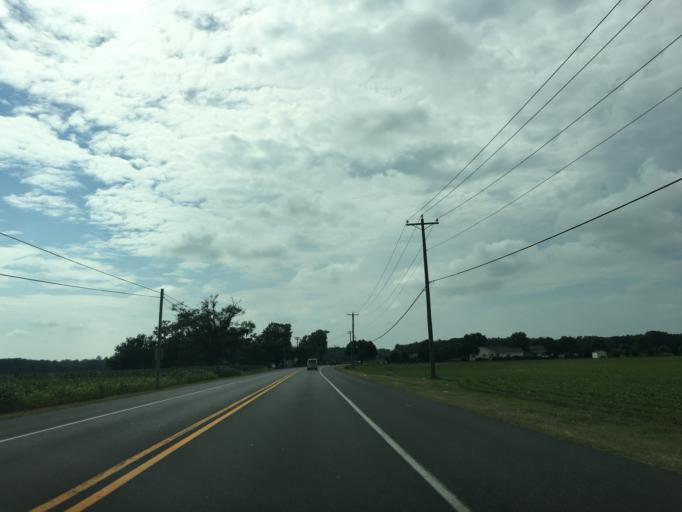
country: US
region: Delaware
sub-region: Sussex County
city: Millsboro
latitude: 38.5553
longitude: -75.2534
